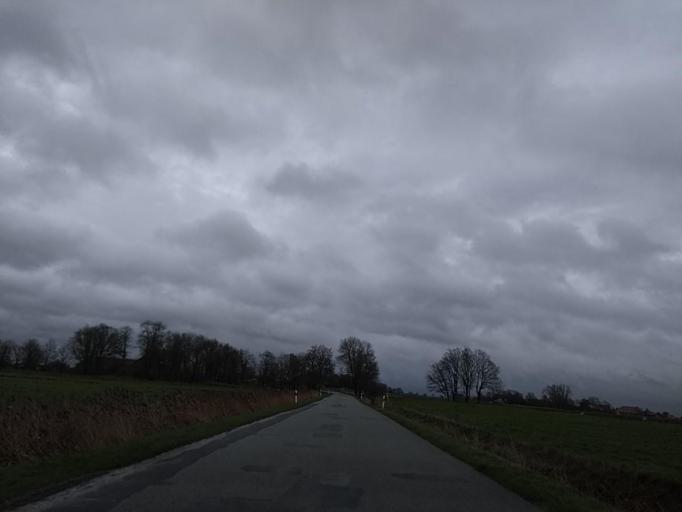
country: DE
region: Lower Saxony
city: Emden
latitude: 53.2896
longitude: 7.2578
